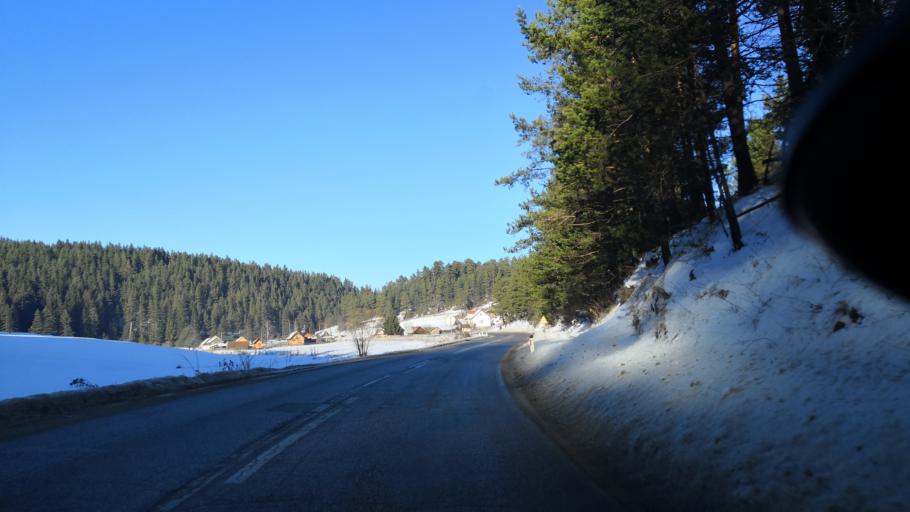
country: BA
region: Republika Srpska
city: Sokolac
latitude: 43.9749
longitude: 18.8568
